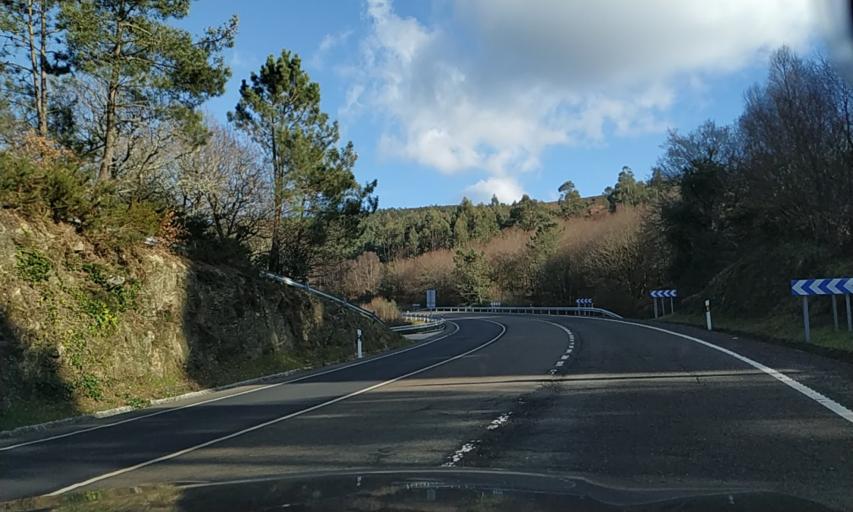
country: ES
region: Galicia
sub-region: Provincia da Coruna
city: Ribeira
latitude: 42.7134
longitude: -8.3719
